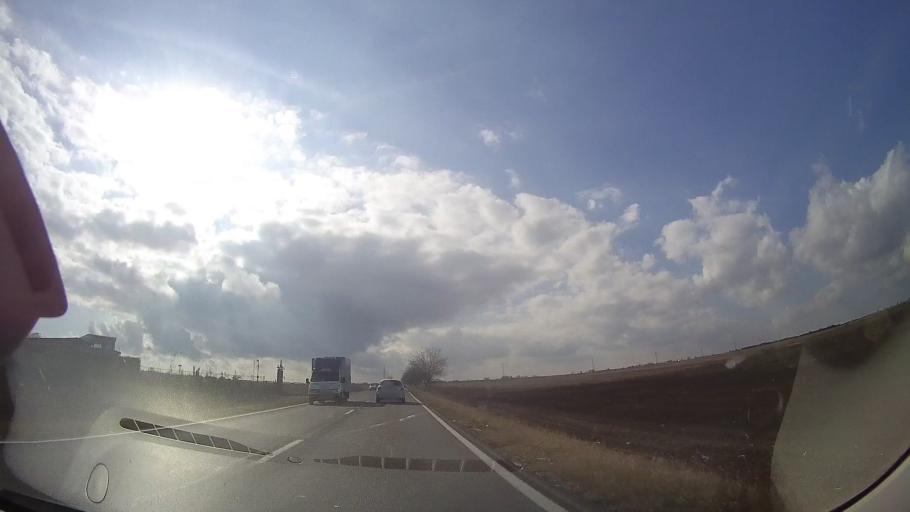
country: RO
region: Constanta
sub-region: Comuna Agigea
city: Agigea
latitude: 44.0786
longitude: 28.6022
